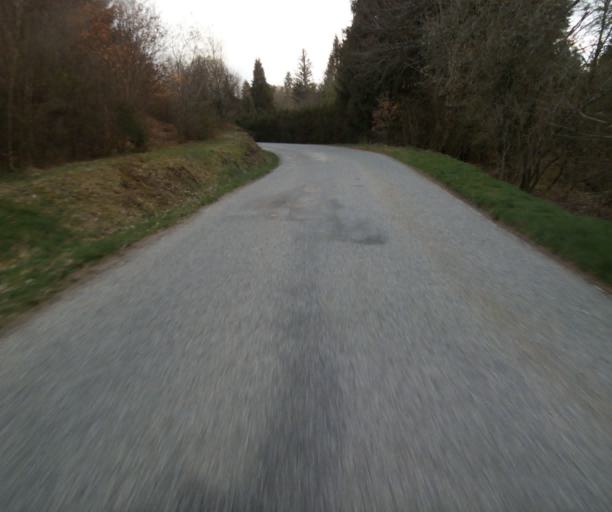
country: FR
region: Limousin
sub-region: Departement de la Correze
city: Correze
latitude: 45.2750
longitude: 1.9746
